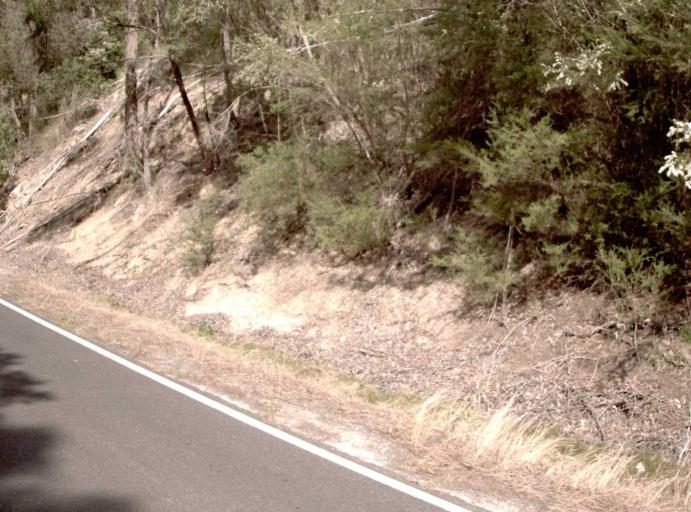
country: AU
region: New South Wales
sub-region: Bega Valley
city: Eden
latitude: -37.4818
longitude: 149.6296
